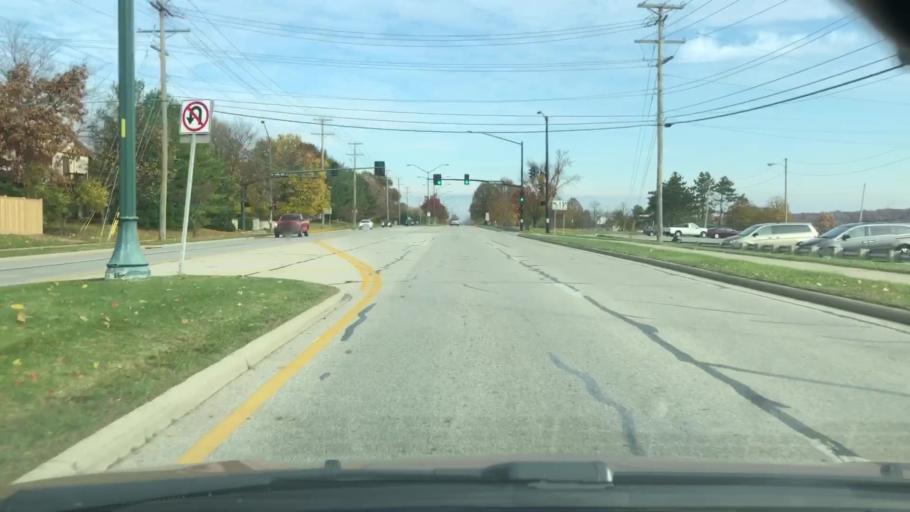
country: US
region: Ohio
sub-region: Franklin County
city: Huber Ridge
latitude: 40.1085
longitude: -82.8872
